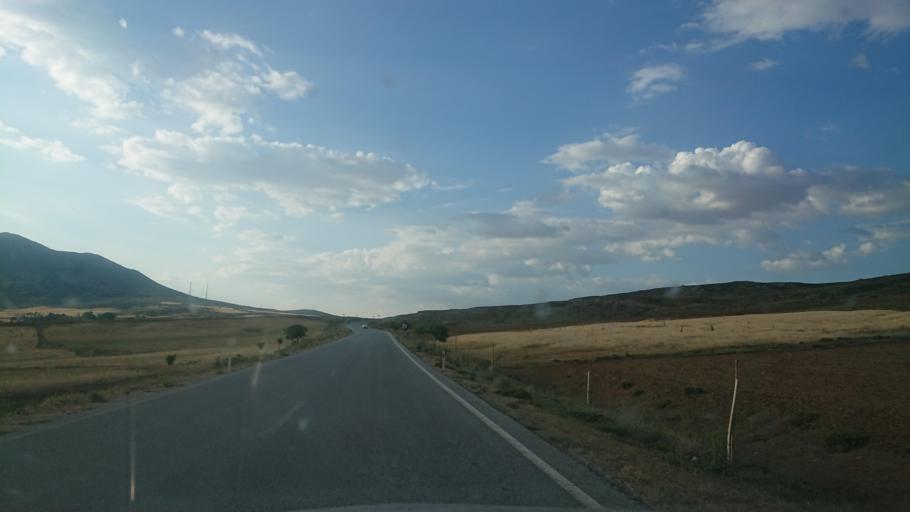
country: TR
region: Aksaray
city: Balci
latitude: 38.6032
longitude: 34.1028
